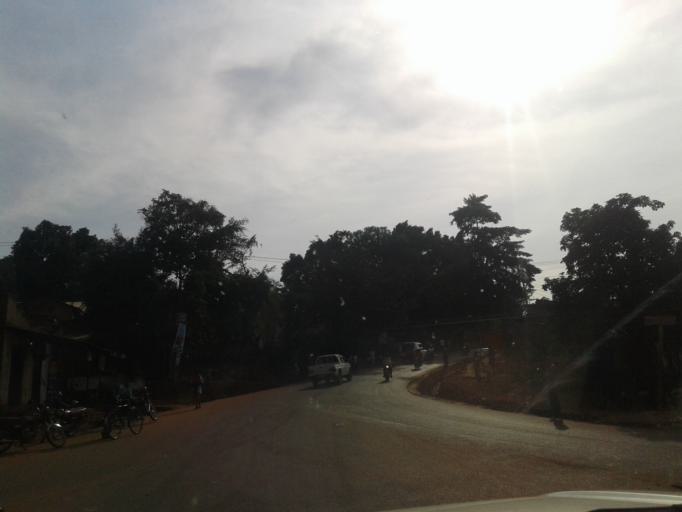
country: UG
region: Central Region
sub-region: Wakiso District
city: Kireka
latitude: 0.3345
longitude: 32.6340
